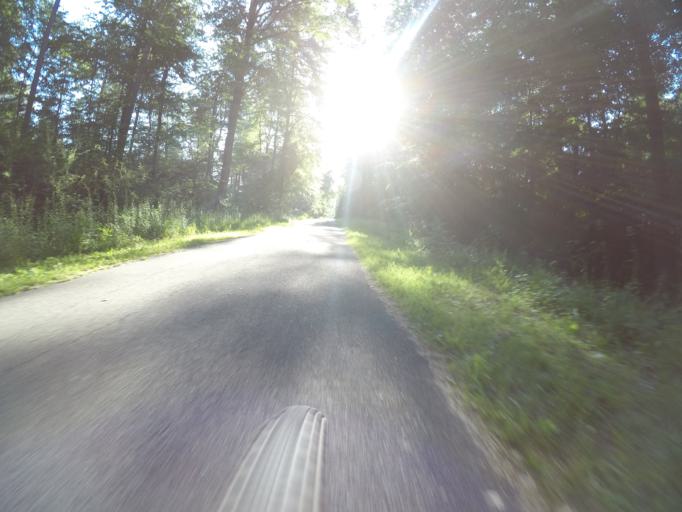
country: DE
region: Baden-Wuerttemberg
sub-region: Regierungsbezirk Stuttgart
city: Sindelfingen
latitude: 48.7197
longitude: 9.0313
